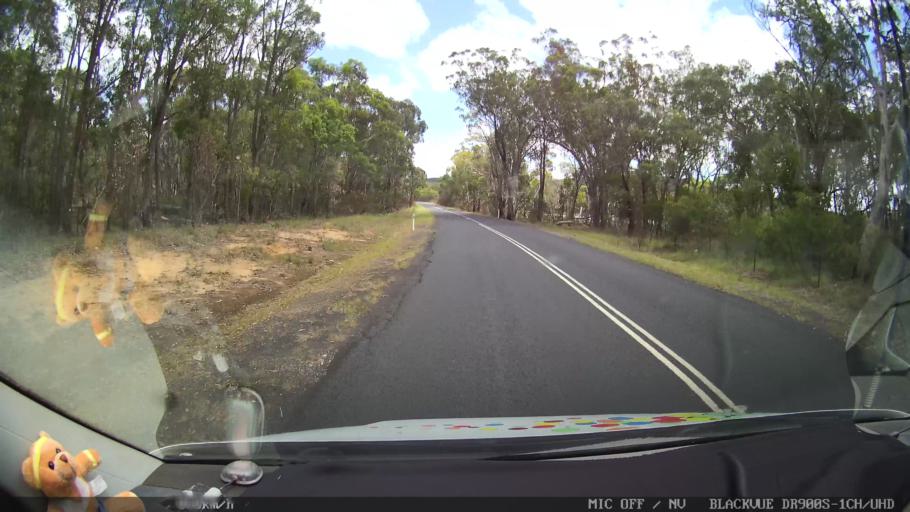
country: AU
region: New South Wales
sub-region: Glen Innes Severn
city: Glen Innes
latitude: -29.4650
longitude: 151.6199
